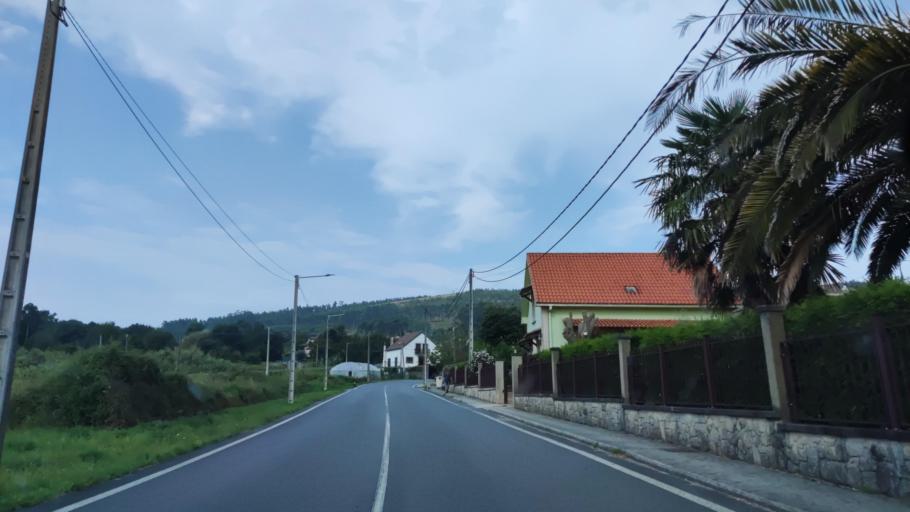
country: ES
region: Galicia
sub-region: Provincia da Coruna
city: Rianxo
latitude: 42.6540
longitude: -8.7701
